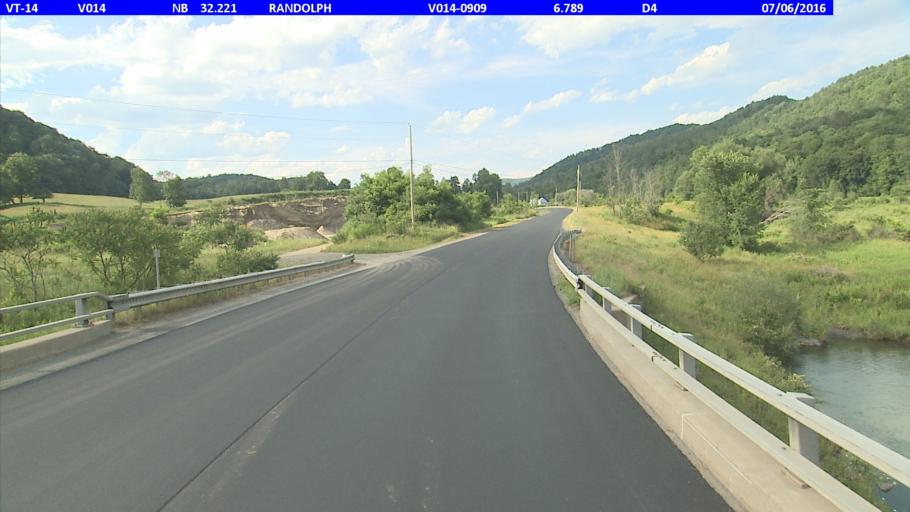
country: US
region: Vermont
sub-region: Orange County
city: Chelsea
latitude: 43.9656
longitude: -72.5549
